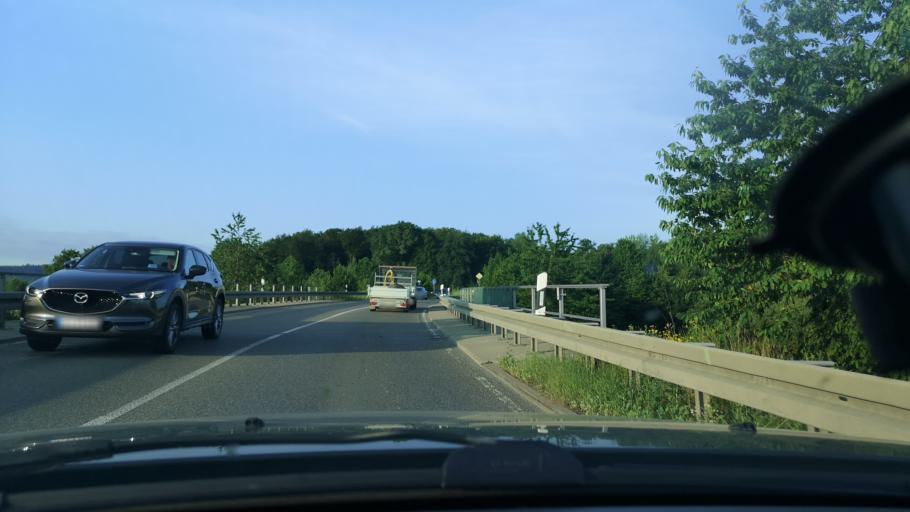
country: DE
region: Baden-Wuerttemberg
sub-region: Regierungsbezirk Stuttgart
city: Salach
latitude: 48.6811
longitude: 9.7223
